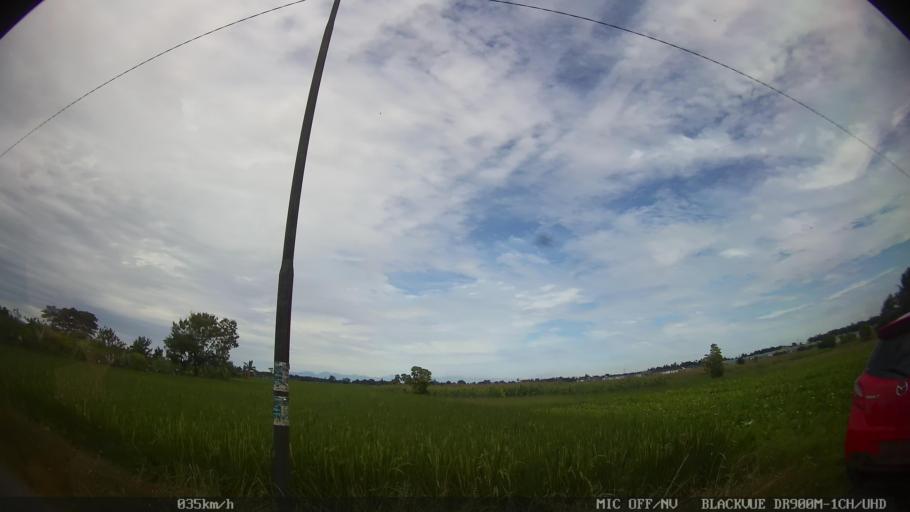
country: ID
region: North Sumatra
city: Sunggal
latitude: 3.5786
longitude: 98.5773
